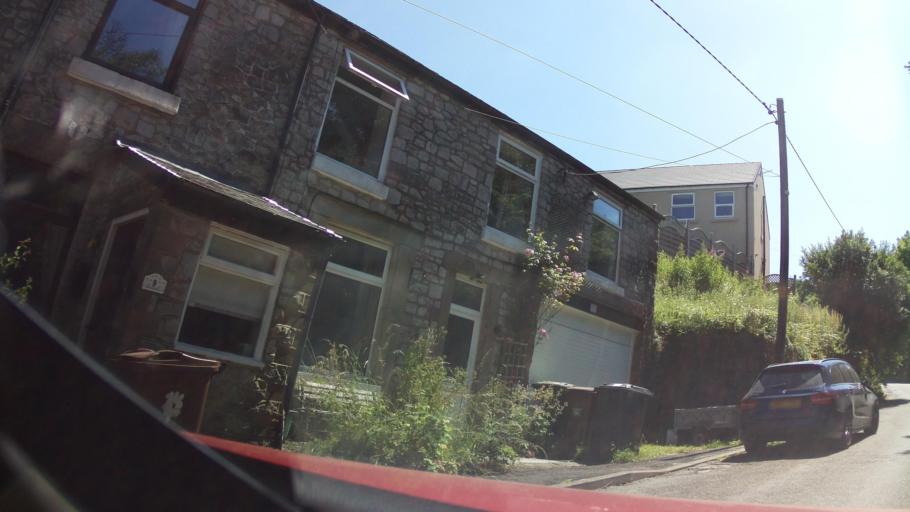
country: GB
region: England
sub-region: Derbyshire
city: Buxton
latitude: 53.2881
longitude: -1.8628
